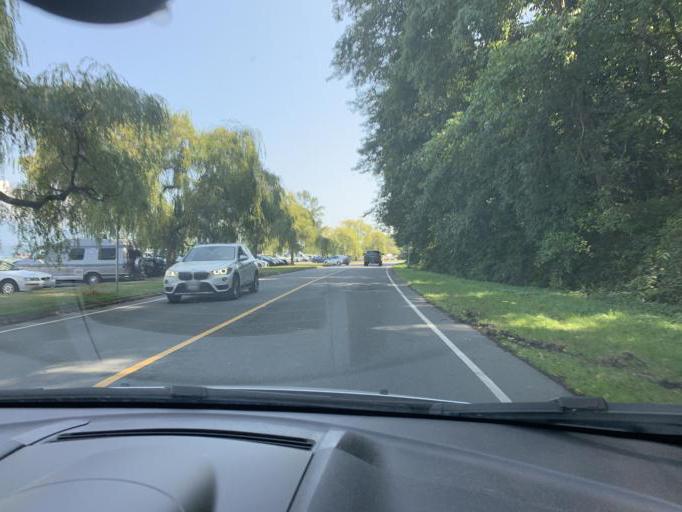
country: CA
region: British Columbia
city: West End
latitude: 49.2782
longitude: -123.2304
